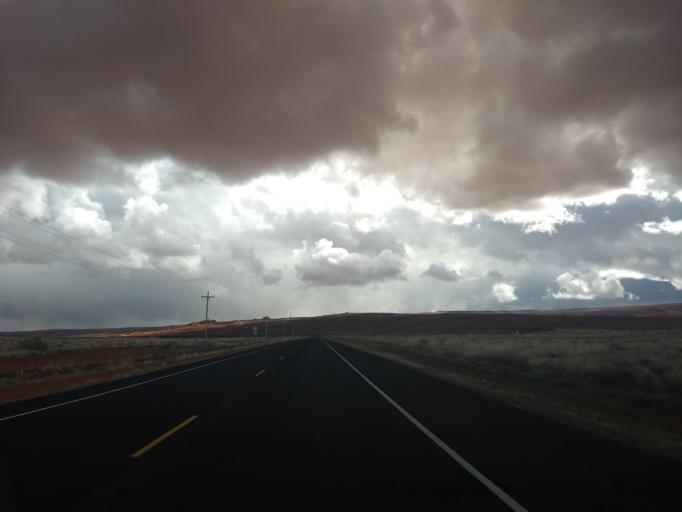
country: US
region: Utah
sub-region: Washington County
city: Hurricane
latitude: 37.1271
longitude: -113.3927
